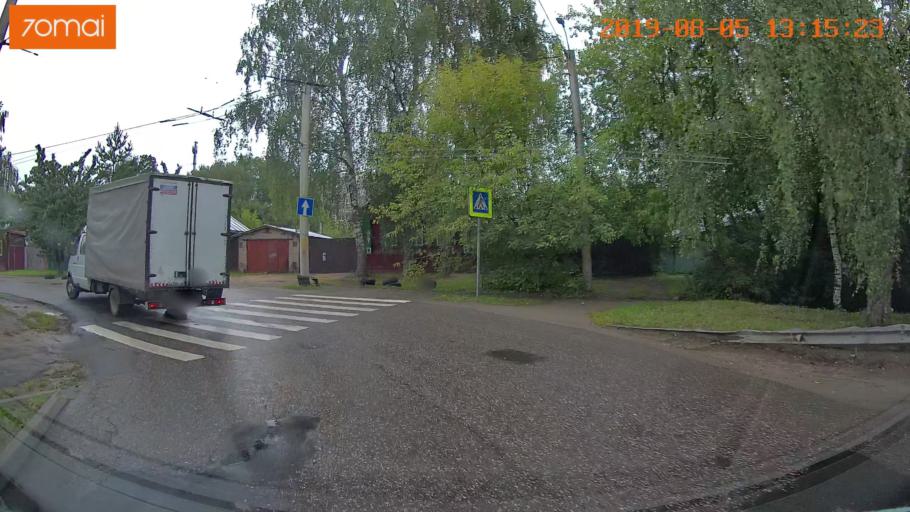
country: RU
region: Ivanovo
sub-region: Gorod Ivanovo
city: Ivanovo
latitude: 56.9936
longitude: 41.0218
